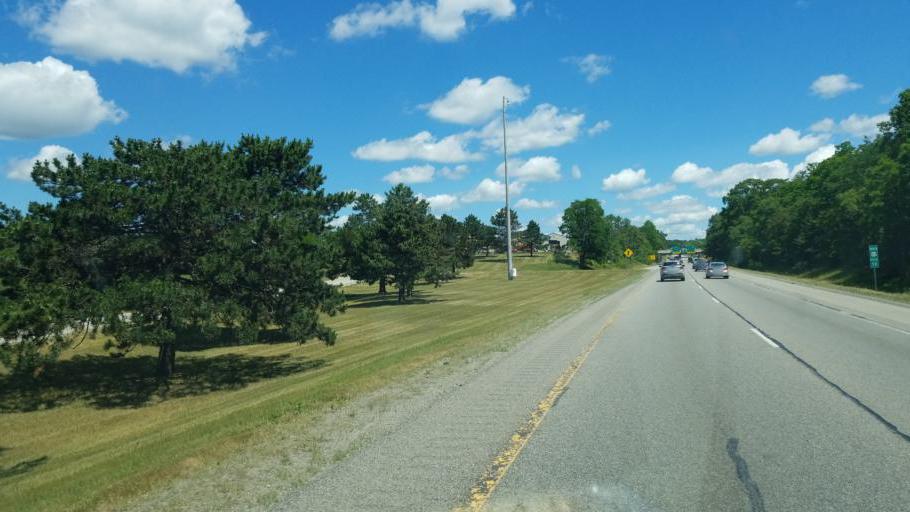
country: US
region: Michigan
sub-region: Livingston County
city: Brighton
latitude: 42.5165
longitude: -83.7572
